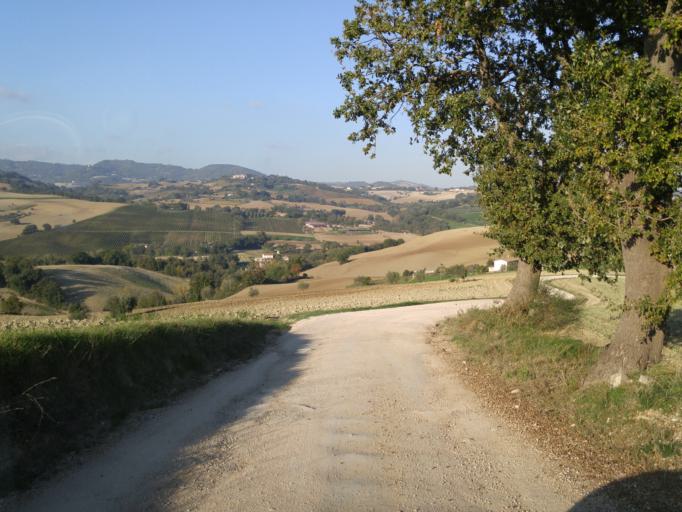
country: IT
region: The Marches
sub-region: Provincia di Pesaro e Urbino
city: Montefelcino
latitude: 43.7169
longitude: 12.8175
